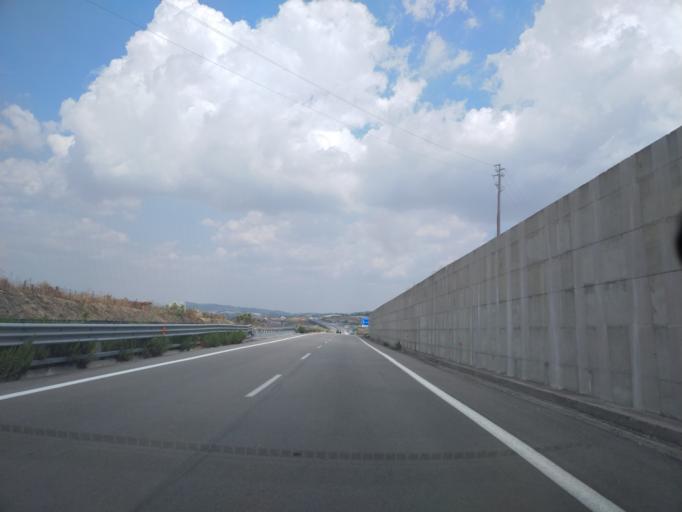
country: IT
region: Sicily
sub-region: Agrigento
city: Castrofilippo
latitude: 37.3784
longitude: 13.7960
